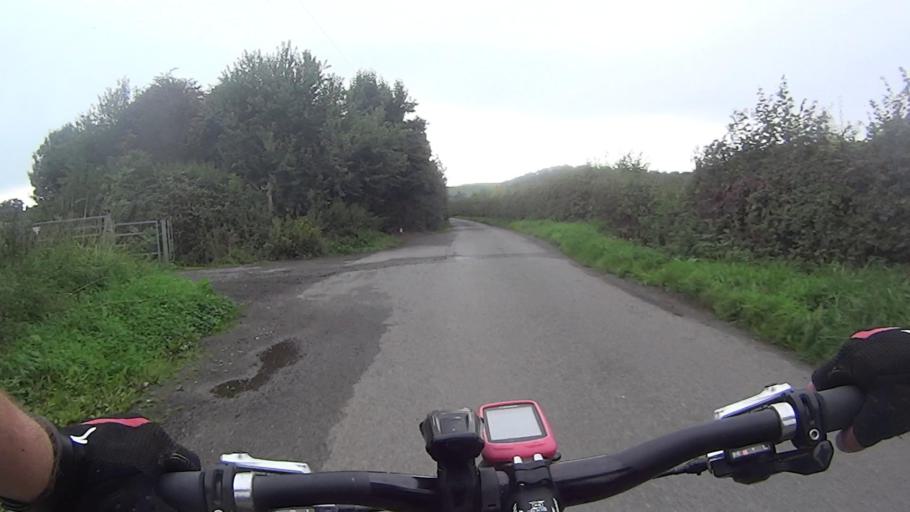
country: GB
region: England
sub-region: Worcestershire
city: Tenbury Wells
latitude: 52.3115
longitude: -2.5675
